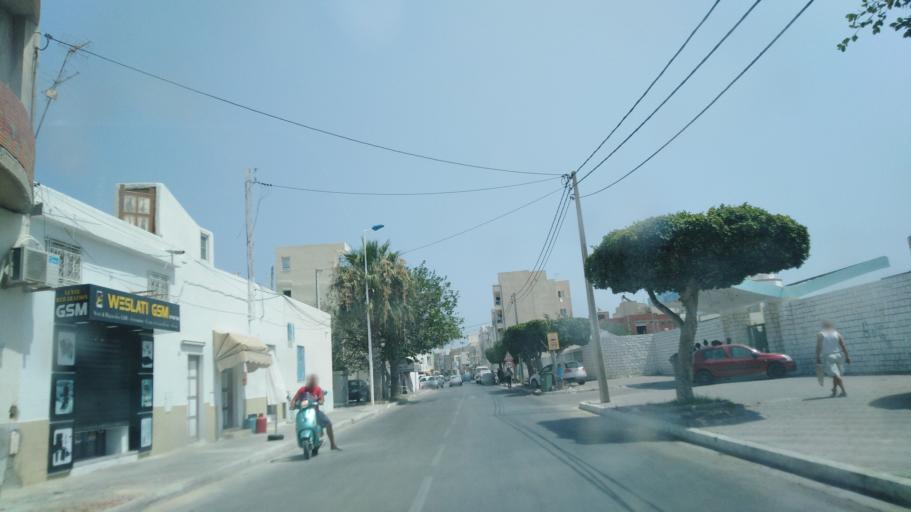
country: TN
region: Al Mahdiyah
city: Mahdia
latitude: 35.5104
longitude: 11.0502
